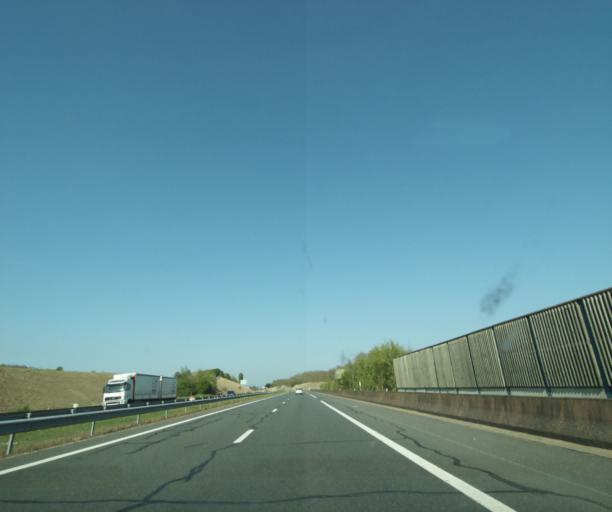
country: FR
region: Centre
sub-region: Departement du Loiret
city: Dordives
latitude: 48.1634
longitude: 2.7602
